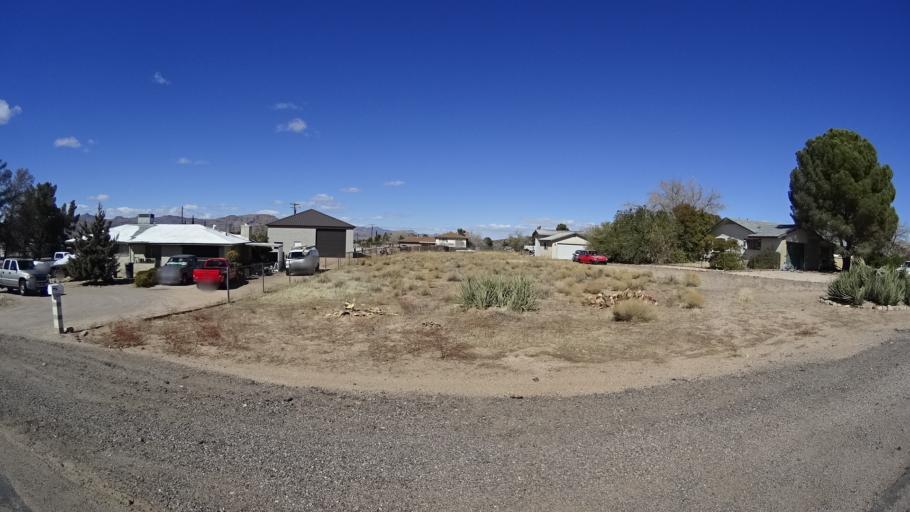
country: US
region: Arizona
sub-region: Mohave County
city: Kingman
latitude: 35.1977
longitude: -114.0049
